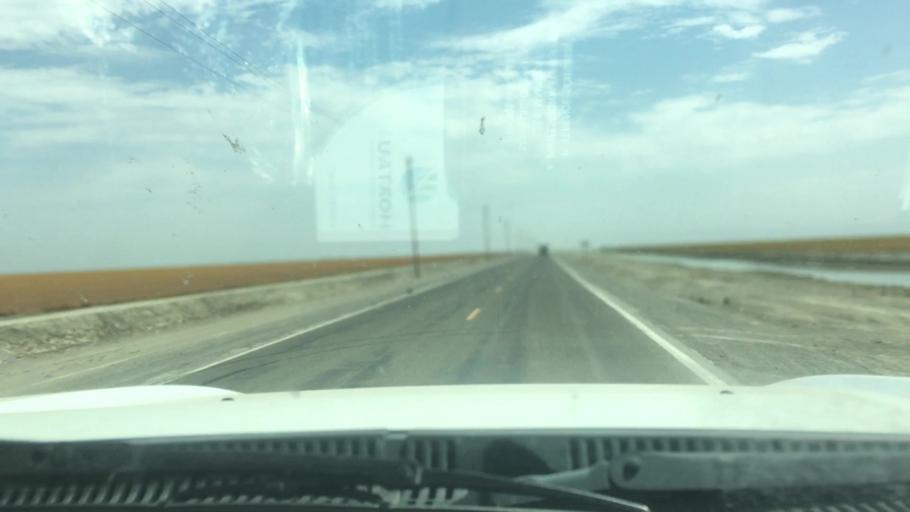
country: US
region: California
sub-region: Tulare County
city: Alpaugh
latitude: 35.9329
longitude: -119.5731
